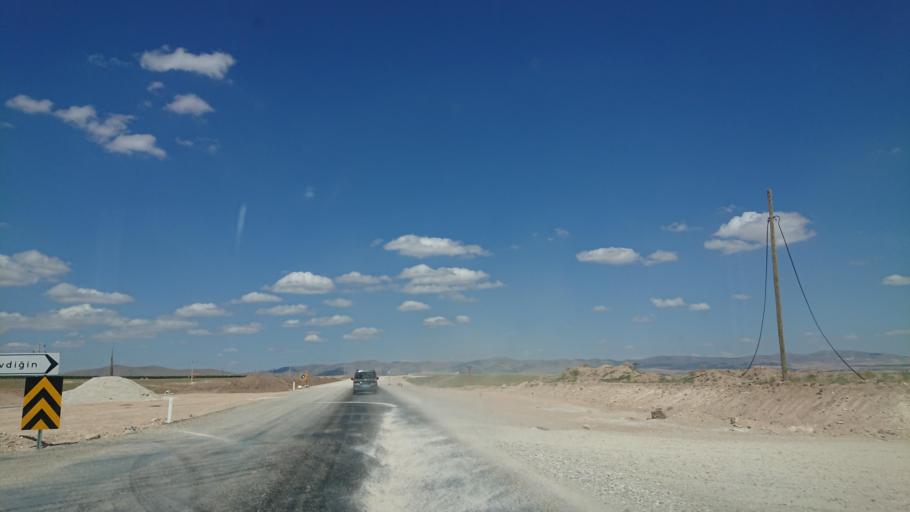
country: TR
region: Kirsehir
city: Kirsehir
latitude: 39.1320
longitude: 34.0424
